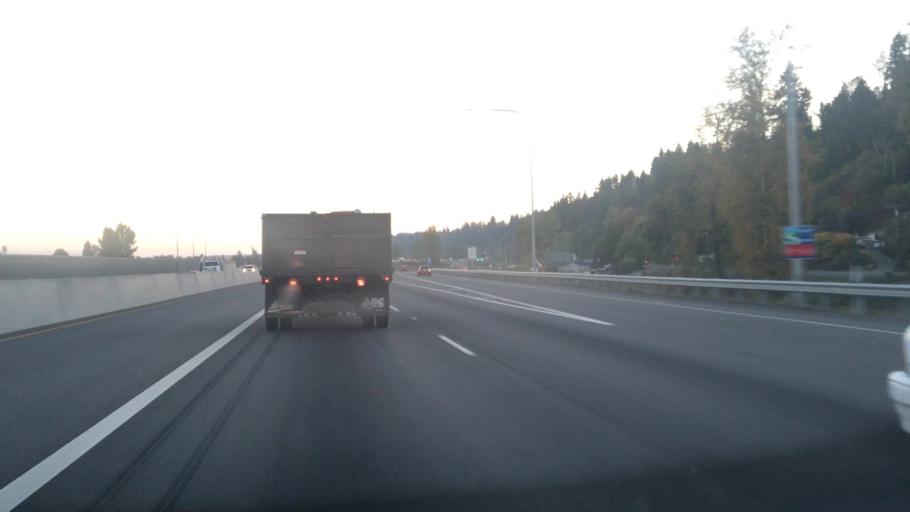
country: US
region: Washington
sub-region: King County
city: Algona
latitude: 47.2779
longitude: -122.2586
